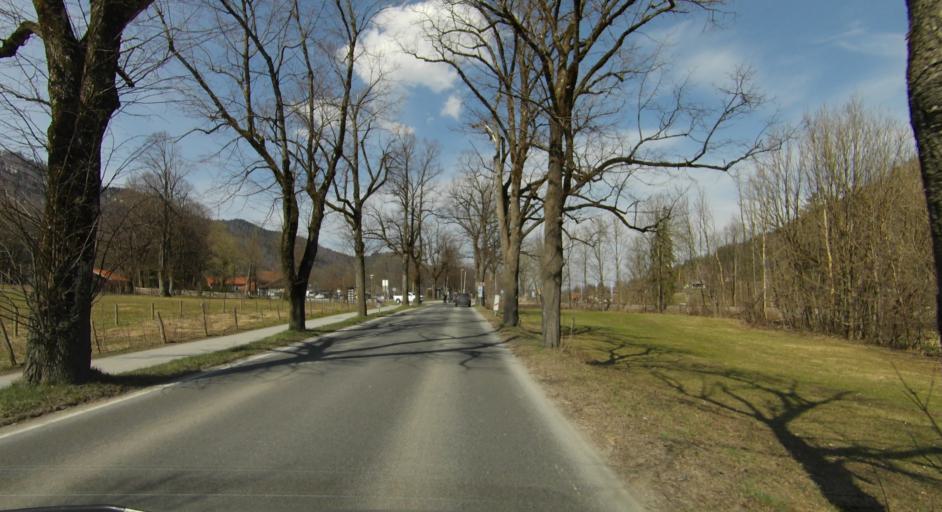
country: DE
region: Bavaria
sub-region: Upper Bavaria
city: Schliersee
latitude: 47.7052
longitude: 11.8764
